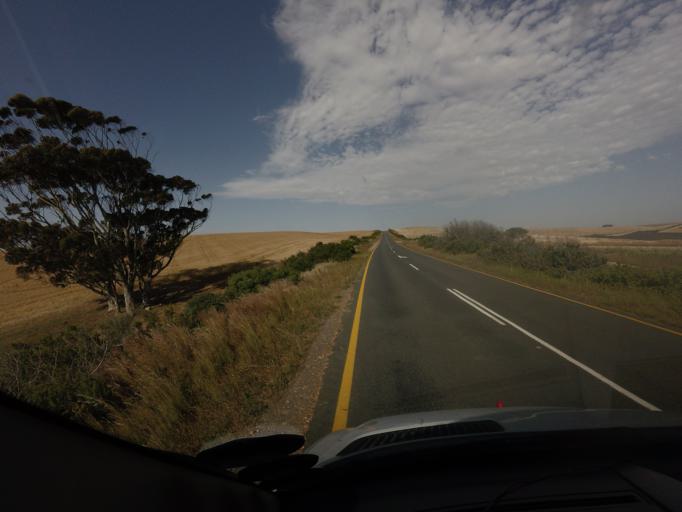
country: ZA
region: Western Cape
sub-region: Overberg District Municipality
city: Caledon
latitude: -34.3302
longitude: 19.7244
